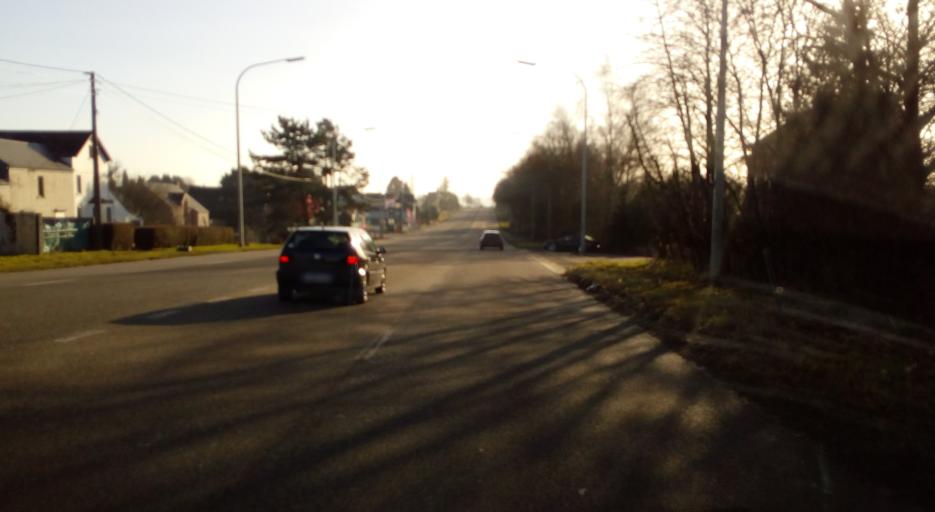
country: BE
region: Wallonia
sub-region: Province du Hainaut
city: Gerpinnes
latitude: 50.3042
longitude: 4.4811
